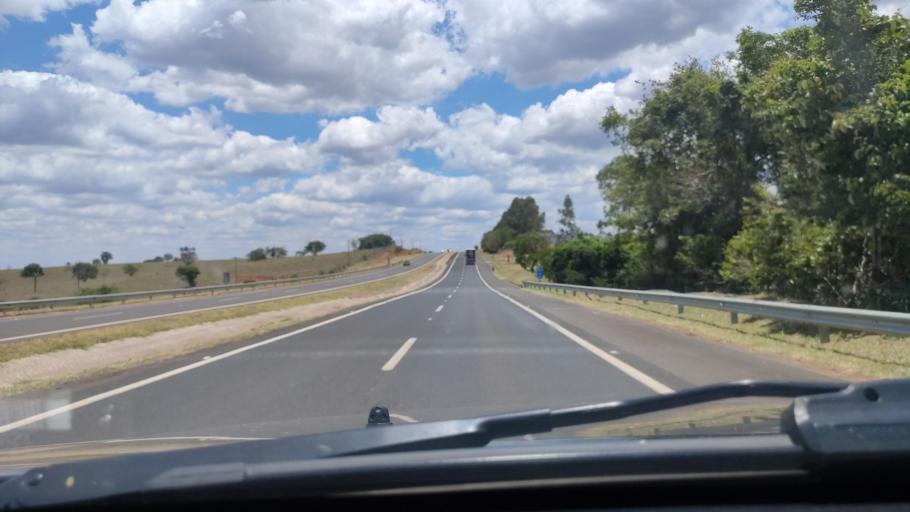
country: BR
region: Sao Paulo
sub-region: Duartina
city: Duartina
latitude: -22.4990
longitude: -49.2714
